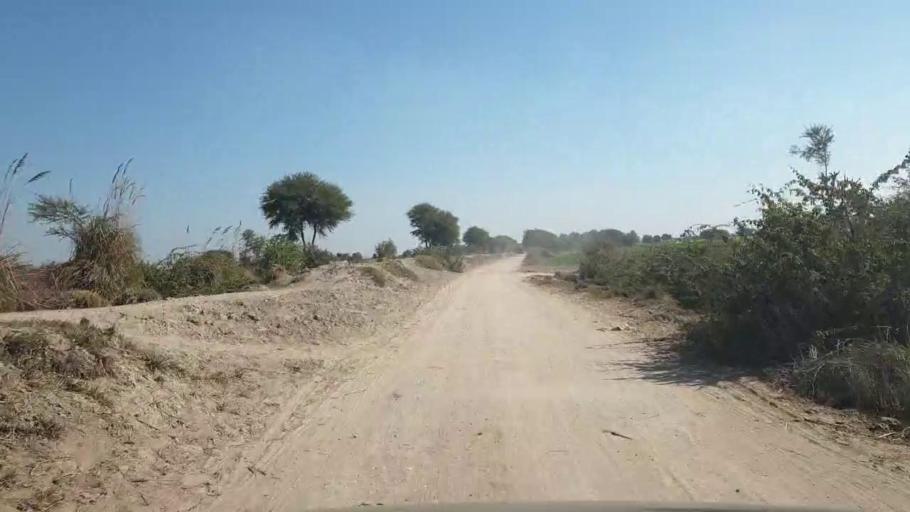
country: PK
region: Sindh
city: Shahpur Chakar
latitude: 26.1432
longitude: 68.6519
